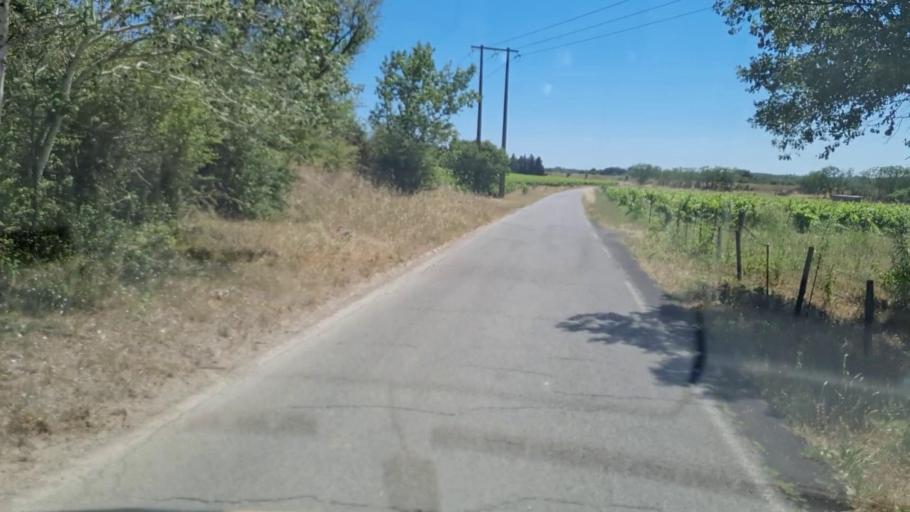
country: FR
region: Languedoc-Roussillon
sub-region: Departement du Gard
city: Vauvert
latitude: 43.6724
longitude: 4.2639
